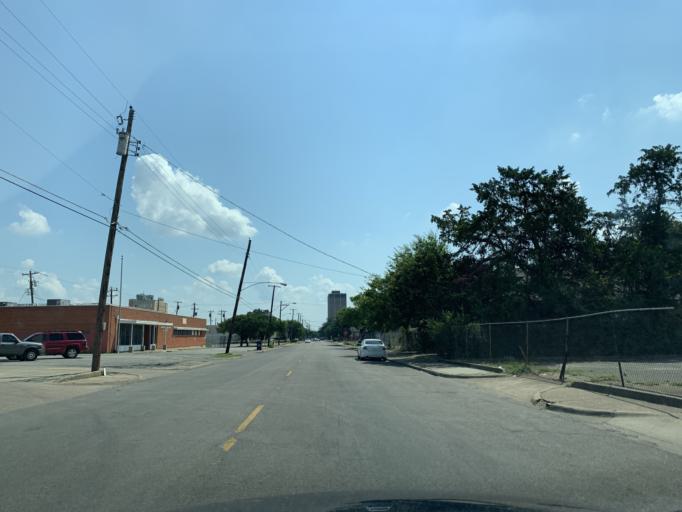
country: US
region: Texas
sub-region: Dallas County
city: Dallas
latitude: 32.7423
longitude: -96.8317
